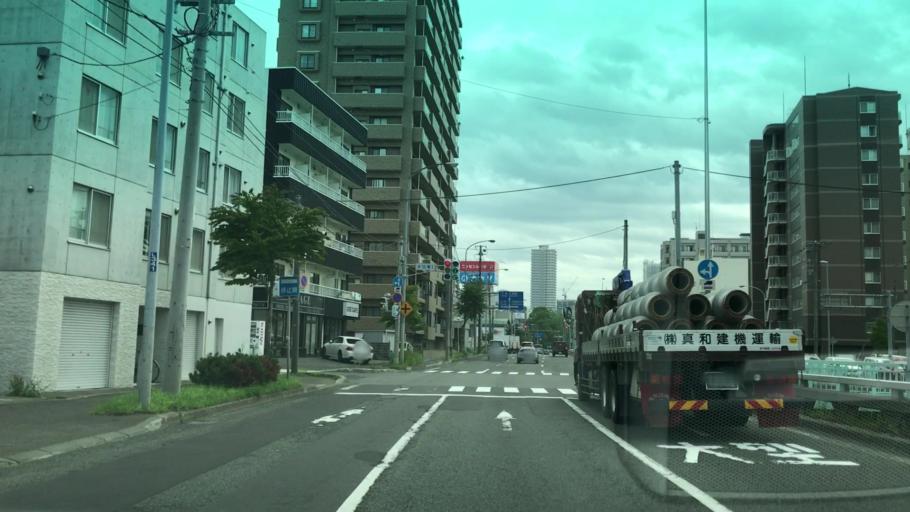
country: JP
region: Hokkaido
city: Sapporo
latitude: 43.0802
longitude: 141.3515
